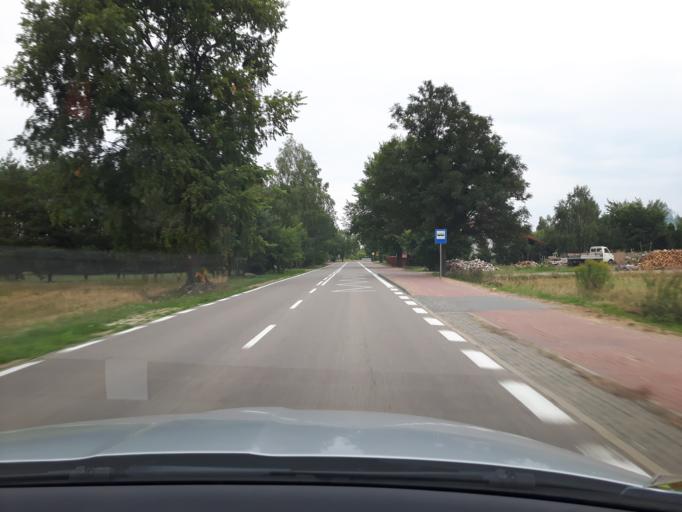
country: PL
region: Masovian Voivodeship
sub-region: Powiat legionowski
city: Wieliszew
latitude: 52.4900
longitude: 20.9607
